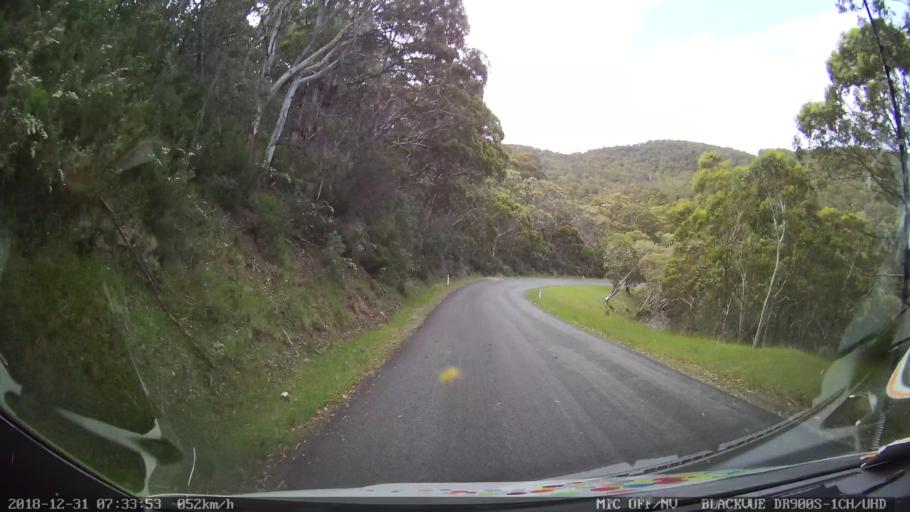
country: AU
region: New South Wales
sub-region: Snowy River
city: Jindabyne
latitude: -36.3343
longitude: 148.4545
